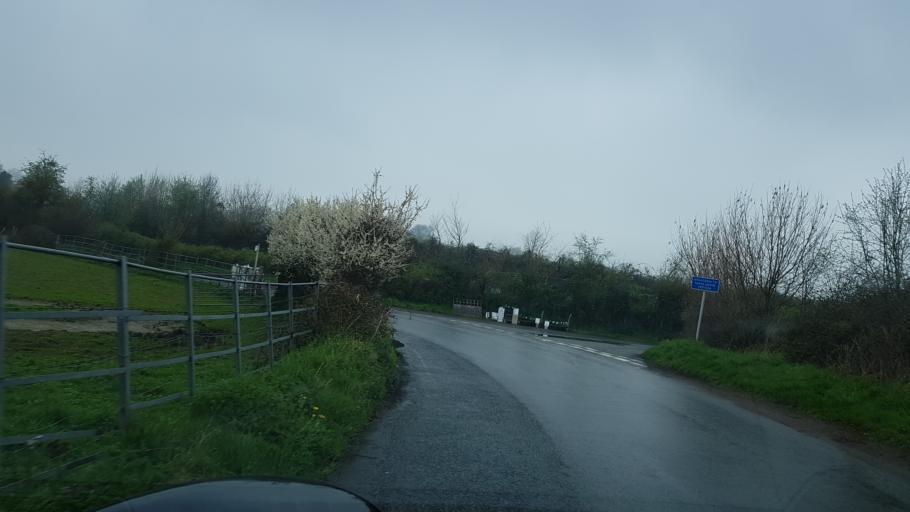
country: GB
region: England
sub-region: Herefordshire
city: Sellack
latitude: 51.9199
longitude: -2.6125
